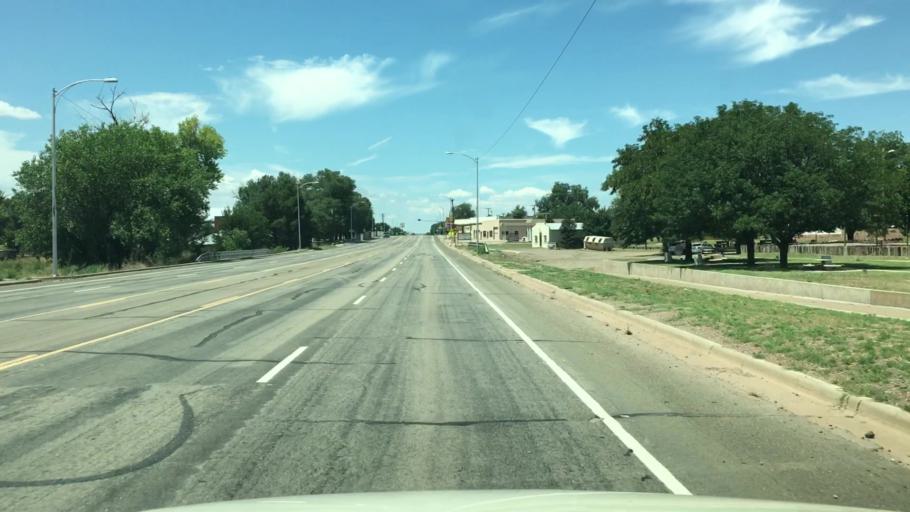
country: US
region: New Mexico
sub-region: De Baca County
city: Fort Sumner
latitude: 34.4684
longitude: -104.2347
